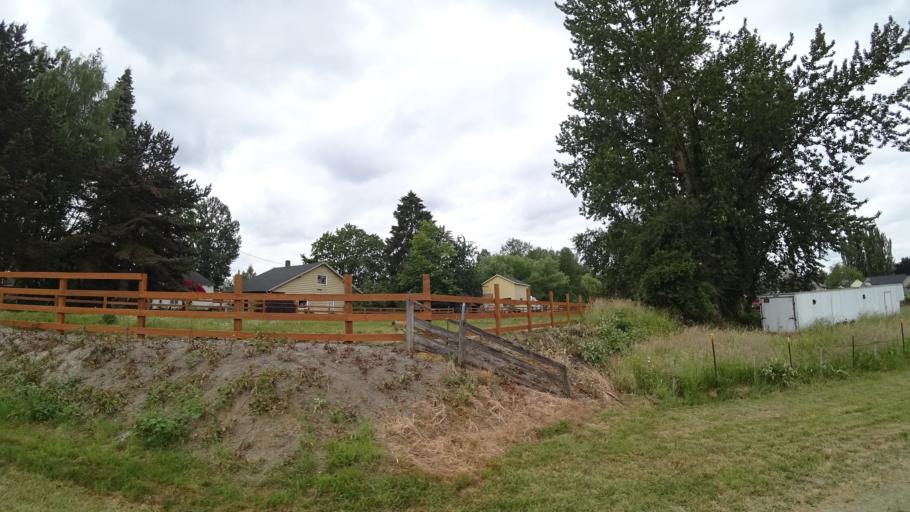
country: US
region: Washington
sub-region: Clark County
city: Vancouver
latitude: 45.5920
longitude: -122.6520
